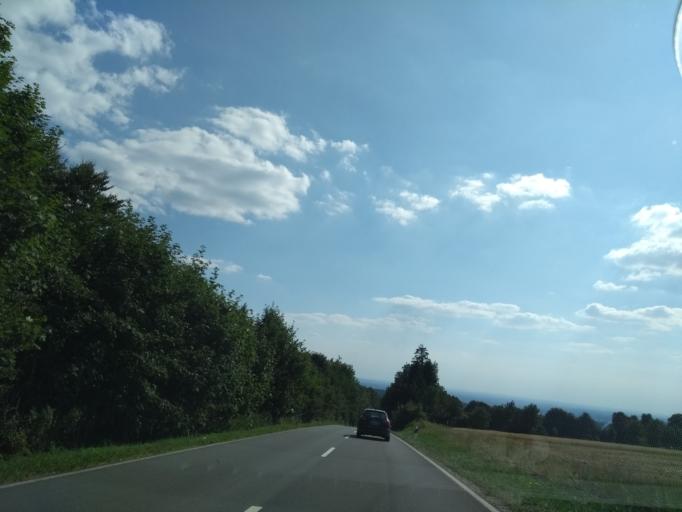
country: DE
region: North Rhine-Westphalia
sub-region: Regierungsbezirk Detmold
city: Altenbeken
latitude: 51.8154
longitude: 8.9089
